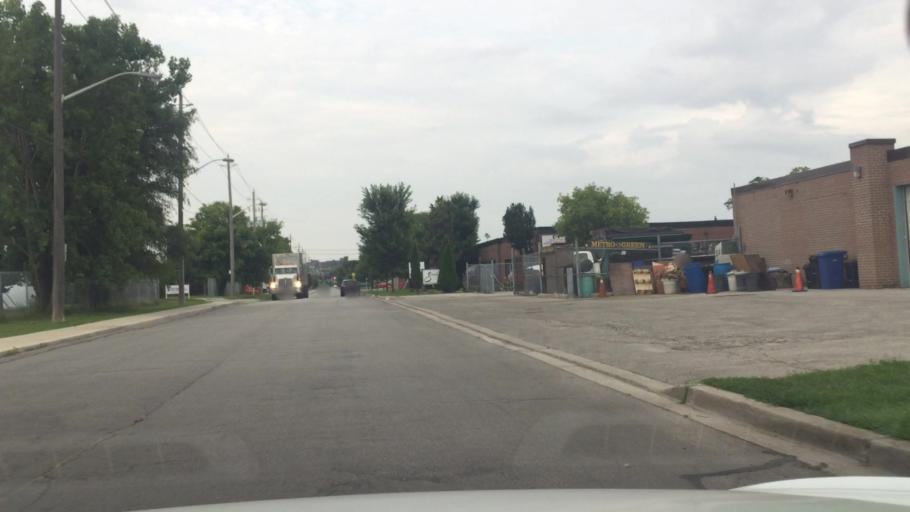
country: CA
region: Ontario
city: Scarborough
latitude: 43.7103
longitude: -79.3164
